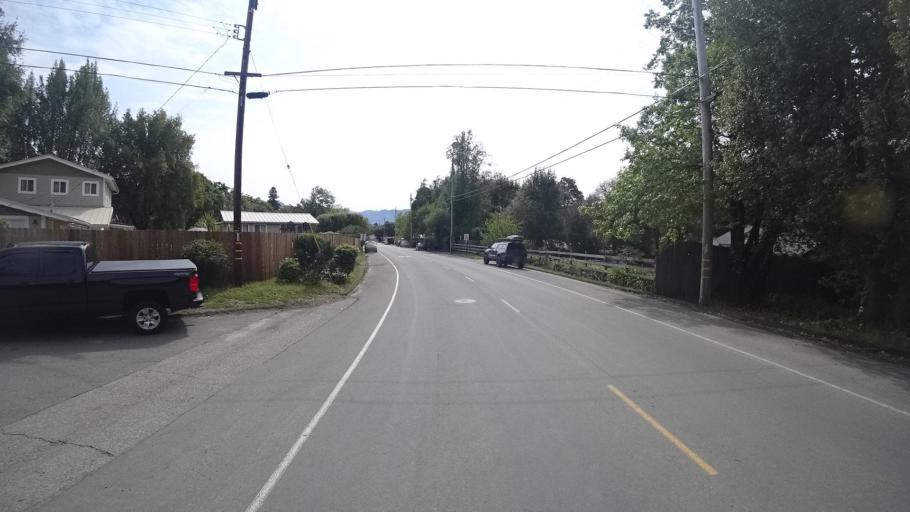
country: US
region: California
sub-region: Humboldt County
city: Redway
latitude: 40.1168
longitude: -123.8267
